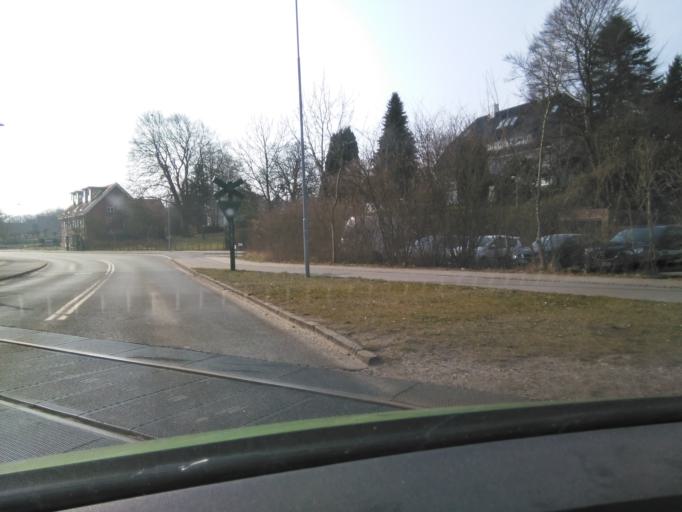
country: DK
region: Central Jutland
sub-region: Arhus Kommune
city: Arhus
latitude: 56.1901
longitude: 10.2389
